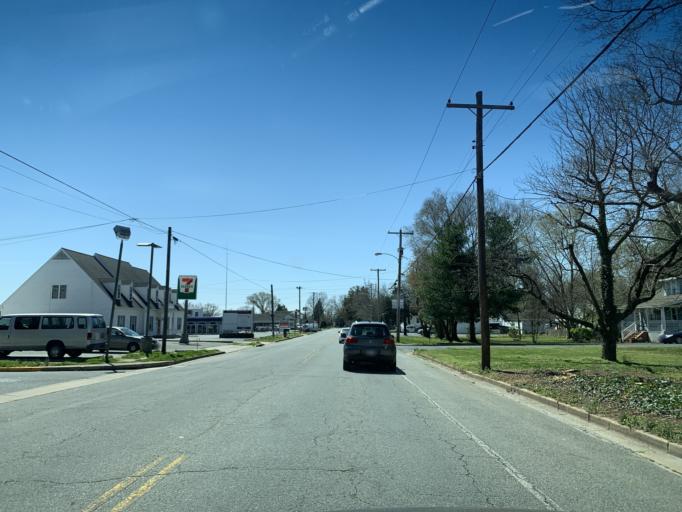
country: US
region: Maryland
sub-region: Talbot County
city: Easton
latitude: 38.7845
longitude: -76.0710
